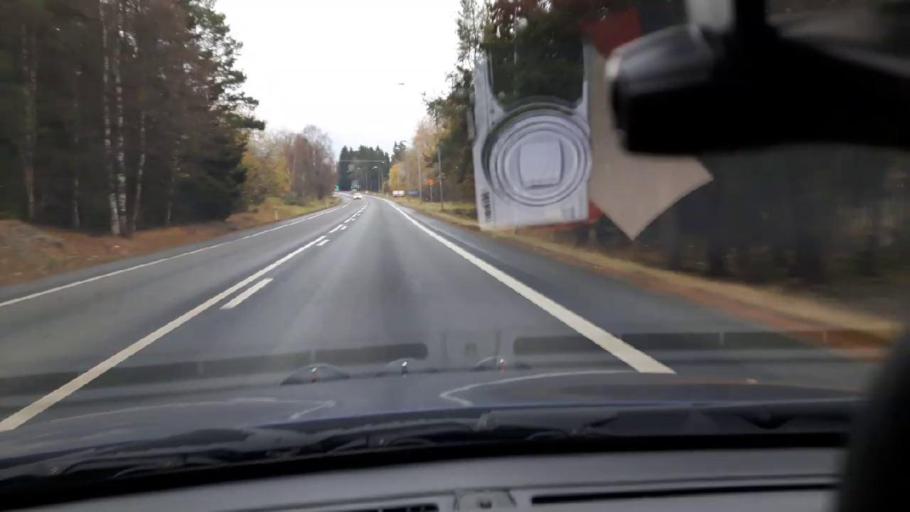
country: SE
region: Jaemtland
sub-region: OEstersunds Kommun
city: Brunflo
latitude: 63.0882
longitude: 14.8103
